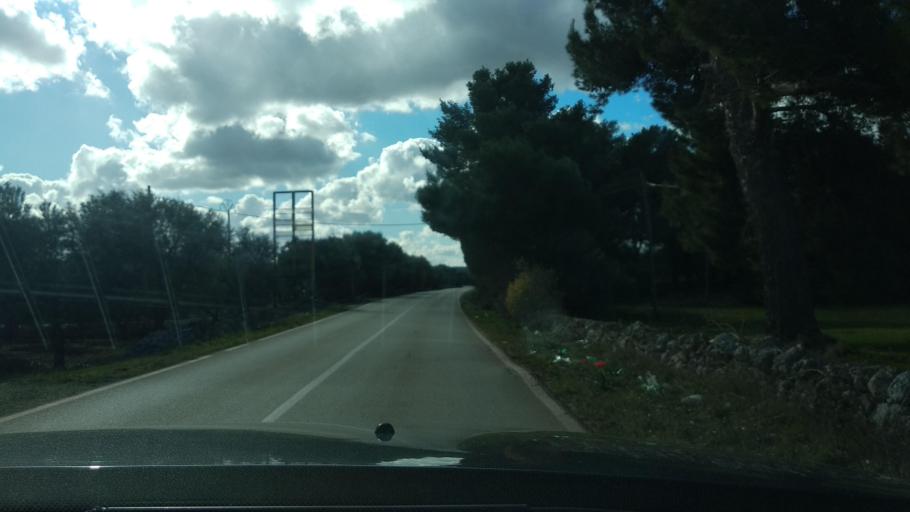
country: IT
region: Apulia
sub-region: Provincia di Brindisi
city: Casalini
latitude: 40.6965
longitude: 17.4832
